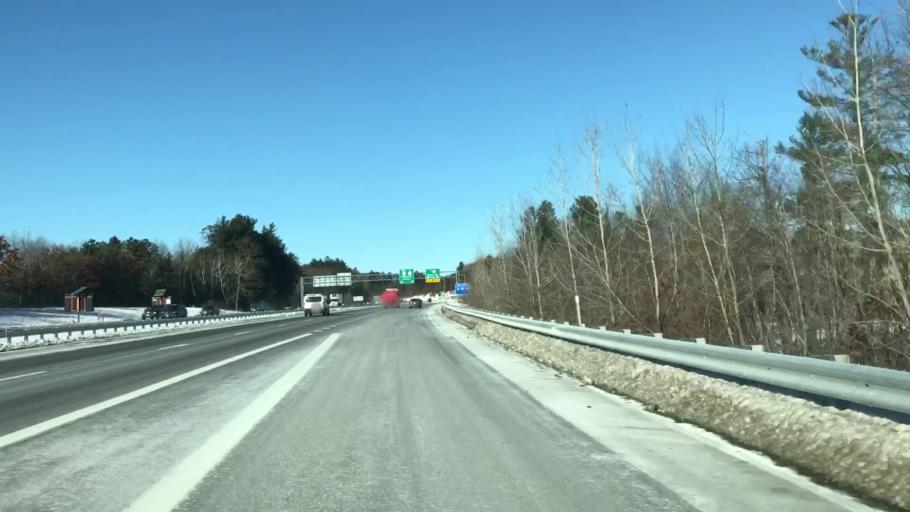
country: US
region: New Hampshire
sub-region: Hillsborough County
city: Bedford
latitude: 42.9534
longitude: -71.4820
